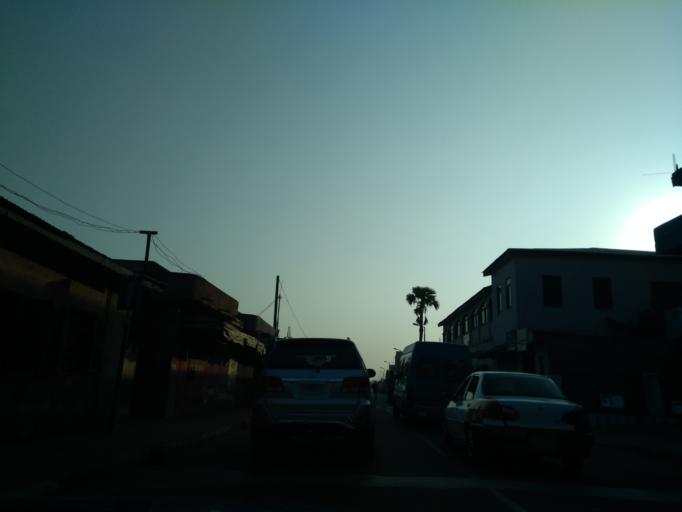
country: GH
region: Greater Accra
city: Accra
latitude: 5.5414
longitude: -0.2121
